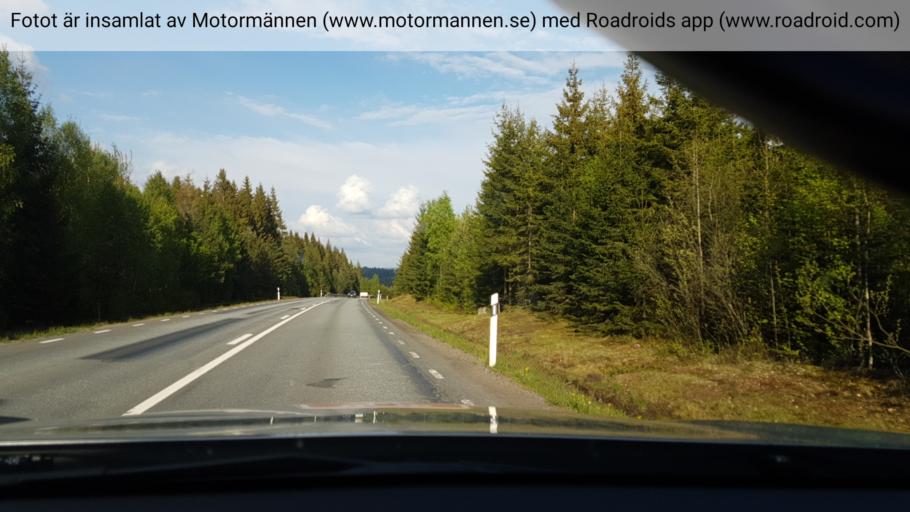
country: SE
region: Joenkoeping
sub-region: Vaggeryds Kommun
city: Skillingaryd
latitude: 57.4158
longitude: 14.0852
